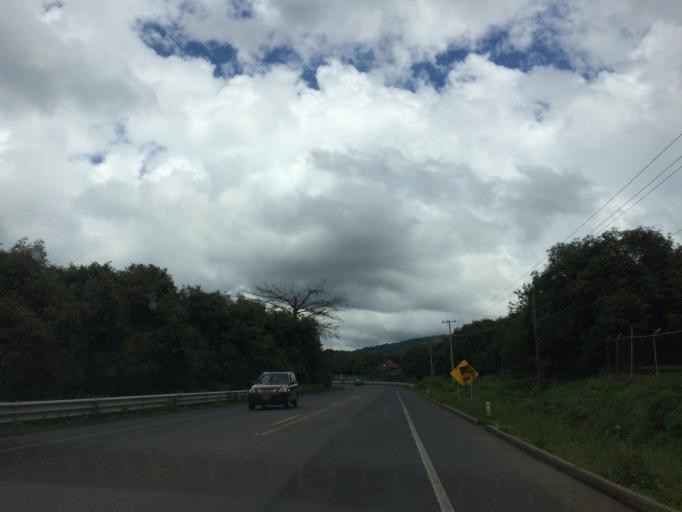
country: MX
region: Michoacan
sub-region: Uruapan
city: Santa Ana Zirosto
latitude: 19.5453
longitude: -102.3319
